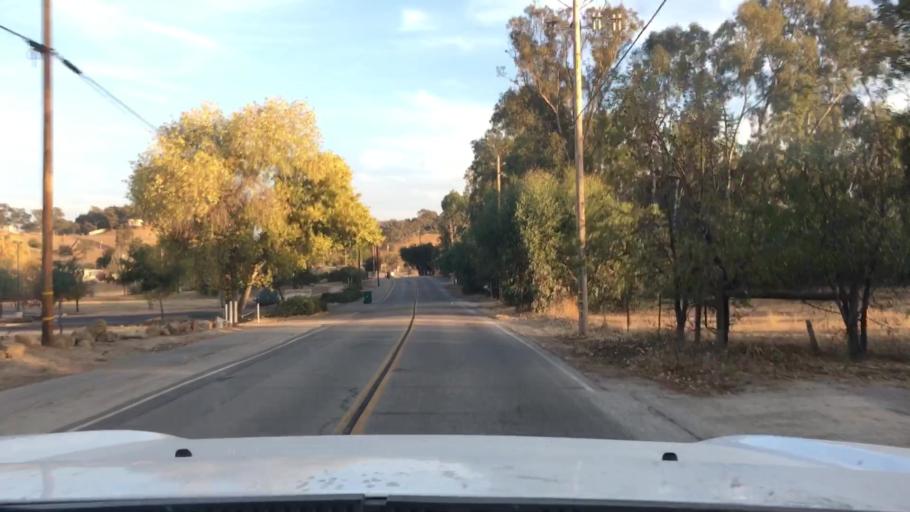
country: US
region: California
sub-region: San Luis Obispo County
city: Atascadero
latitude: 35.4610
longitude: -120.6730
